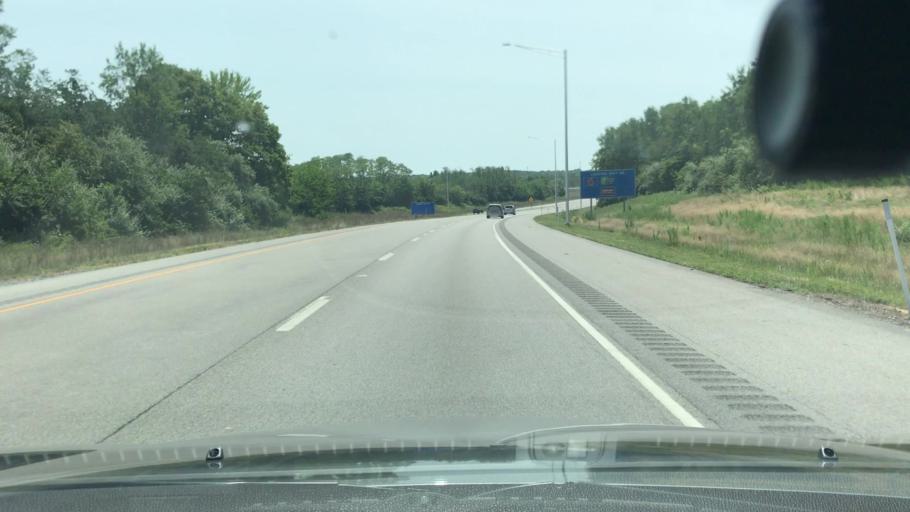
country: US
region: Illinois
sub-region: Jefferson County
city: Mount Vernon
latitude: 38.3355
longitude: -88.9582
